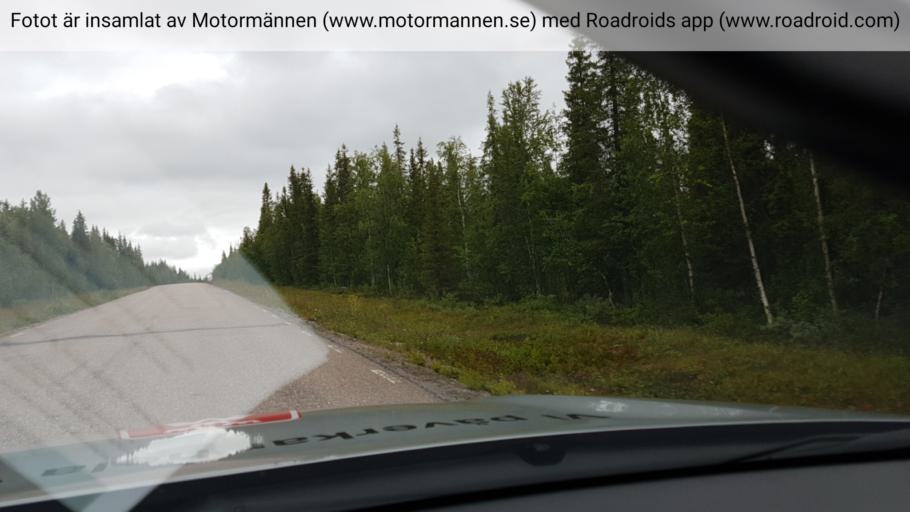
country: SE
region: Norrbotten
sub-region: Overkalix Kommun
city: OEverkalix
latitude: 67.0397
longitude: 22.0375
